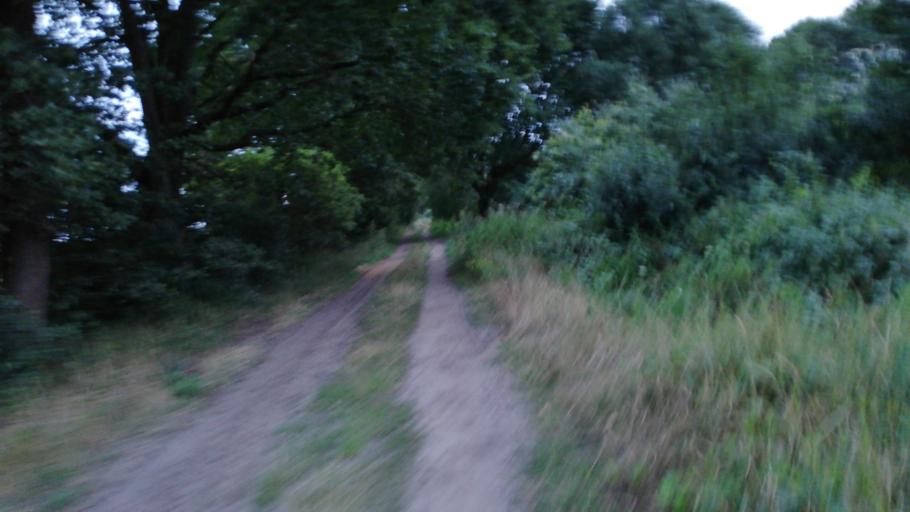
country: DE
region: Lower Saxony
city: Neu Wulmstorf
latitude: 53.4765
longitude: 9.8105
